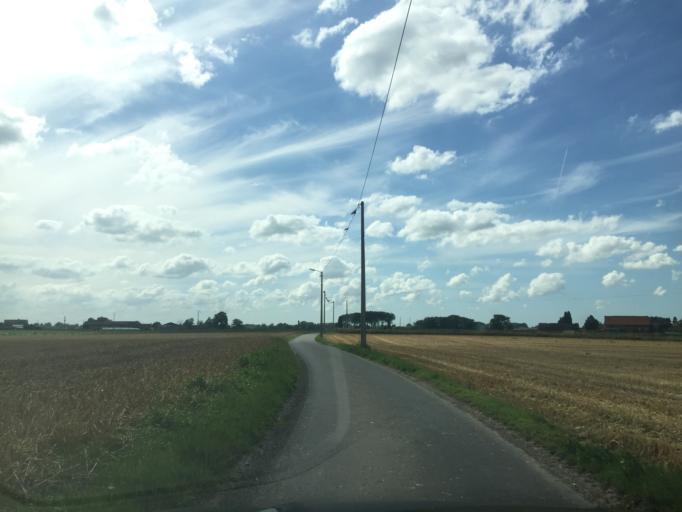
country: BE
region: Flanders
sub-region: Provincie West-Vlaanderen
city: Staden
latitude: 50.9844
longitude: 3.0432
